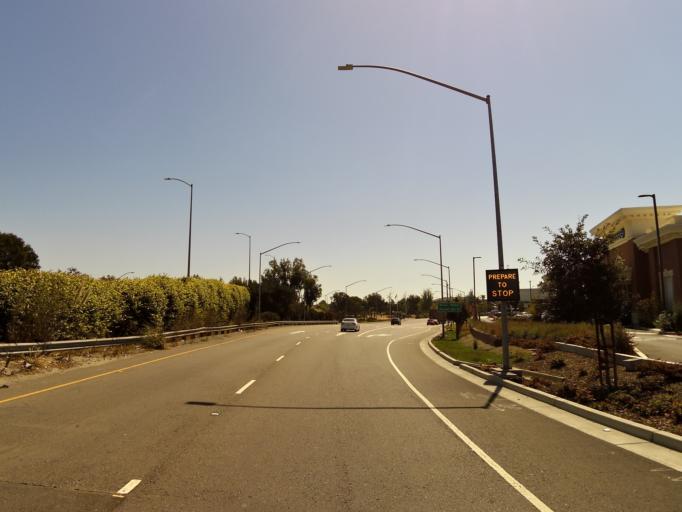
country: US
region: California
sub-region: Alameda County
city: Oakland
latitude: 37.7850
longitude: -122.2774
